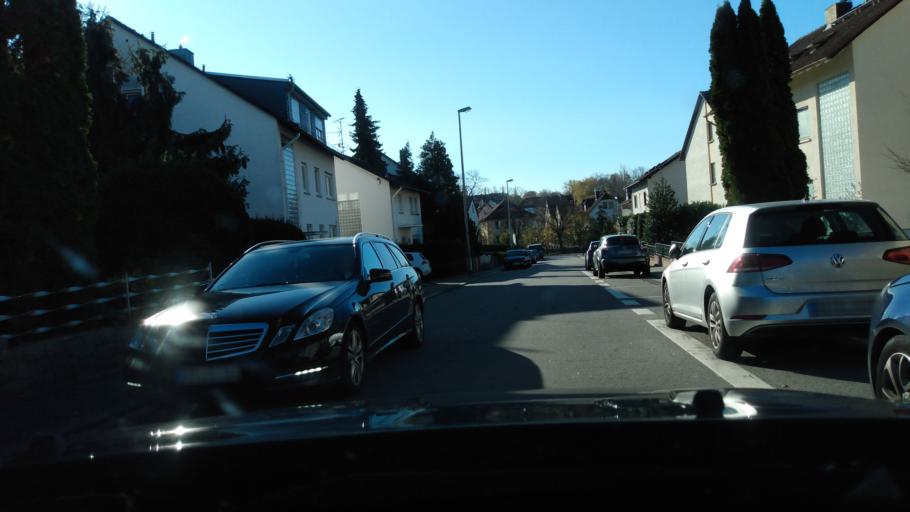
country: DE
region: Hesse
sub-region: Regierungsbezirk Darmstadt
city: Hofheim am Taunus
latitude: 50.0848
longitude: 8.4586
